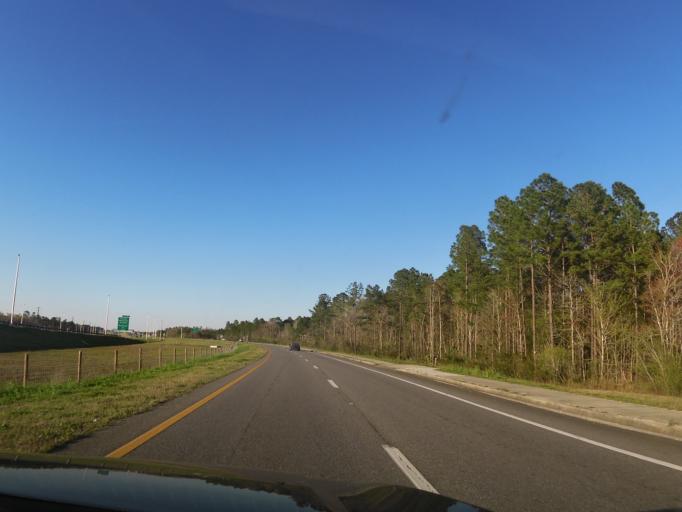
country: US
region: Florida
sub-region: Clay County
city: Middleburg
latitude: 30.1170
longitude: -81.8303
